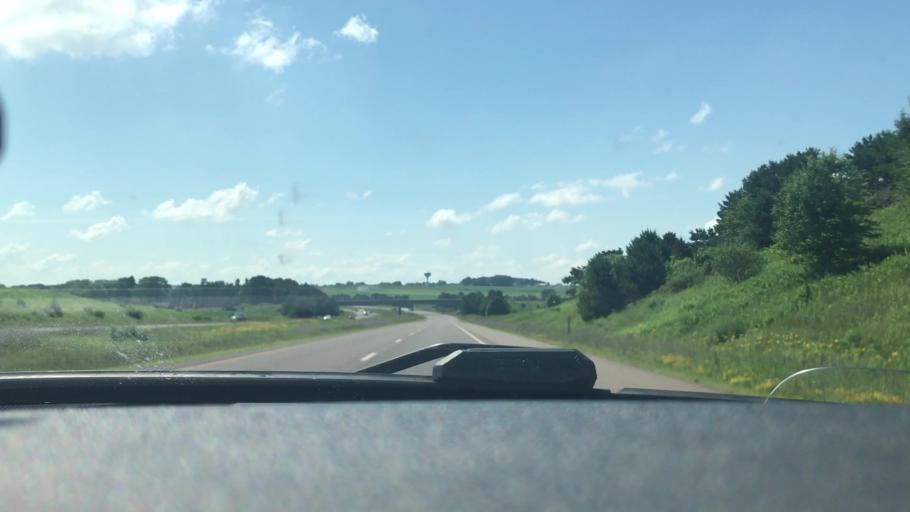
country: US
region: Wisconsin
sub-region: Chippewa County
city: Bloomer
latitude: 45.1149
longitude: -91.5188
